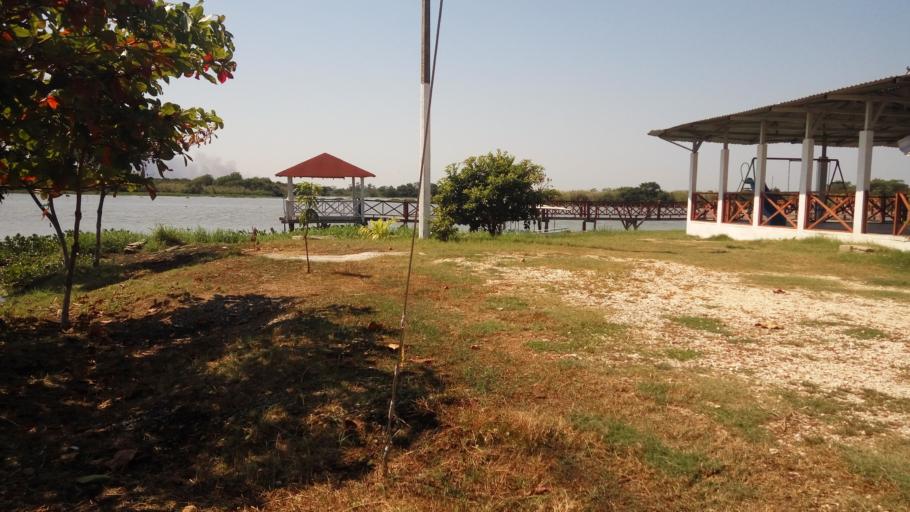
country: MX
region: Tabasco
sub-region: Centla
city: Ignacio Zaragoza
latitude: 18.3988
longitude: -92.9567
